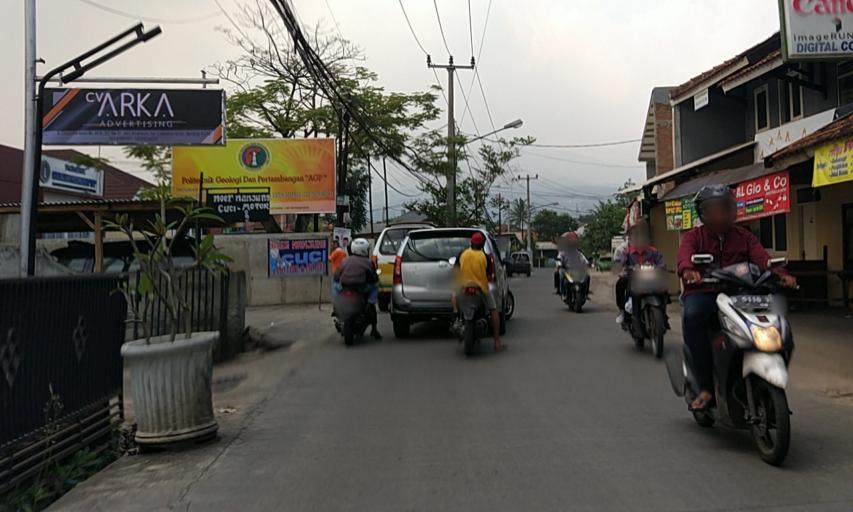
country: ID
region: West Java
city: Bandung
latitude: -6.9175
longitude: 107.6842
